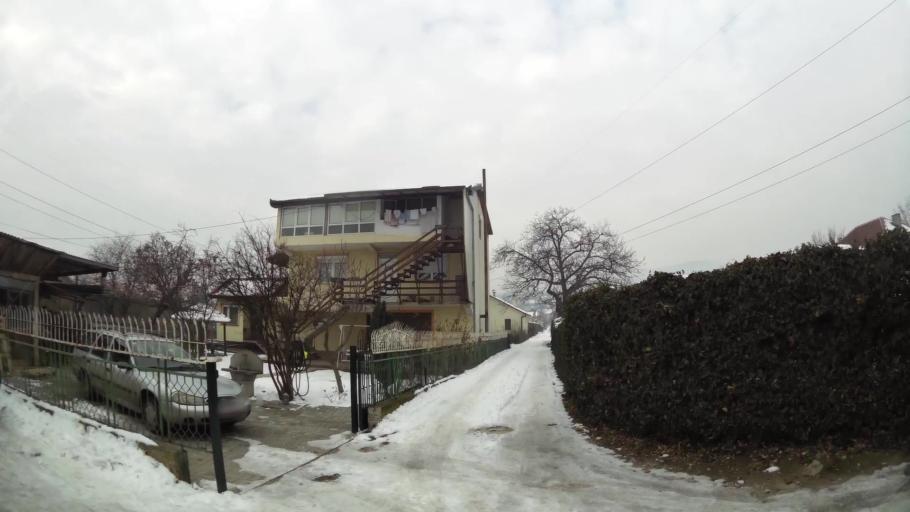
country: MK
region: Saraj
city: Saraj
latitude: 42.0410
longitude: 21.3510
